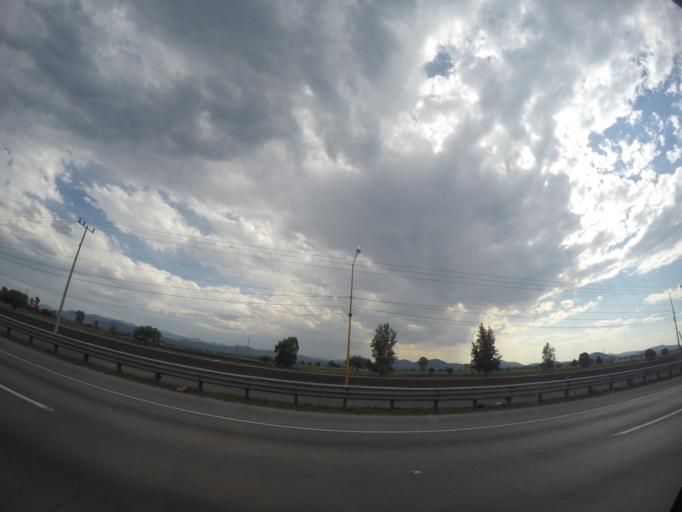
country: MX
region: Queretaro
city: La Estancia
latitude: 20.4226
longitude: -100.0513
